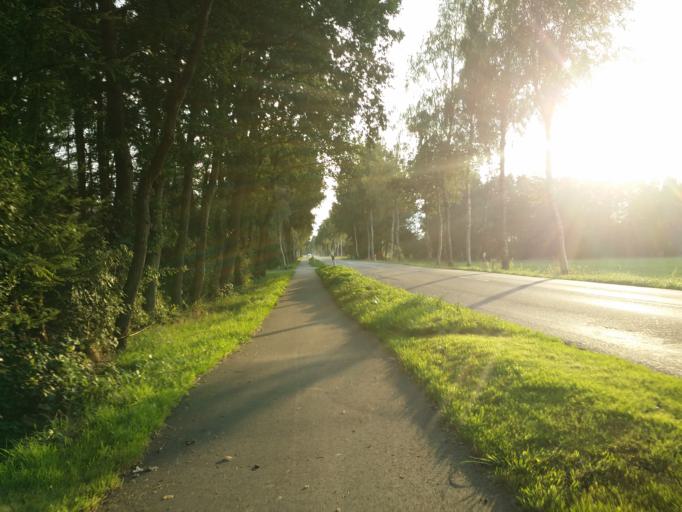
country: DE
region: Lower Saxony
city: Oerel
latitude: 53.4341
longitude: 9.0712
